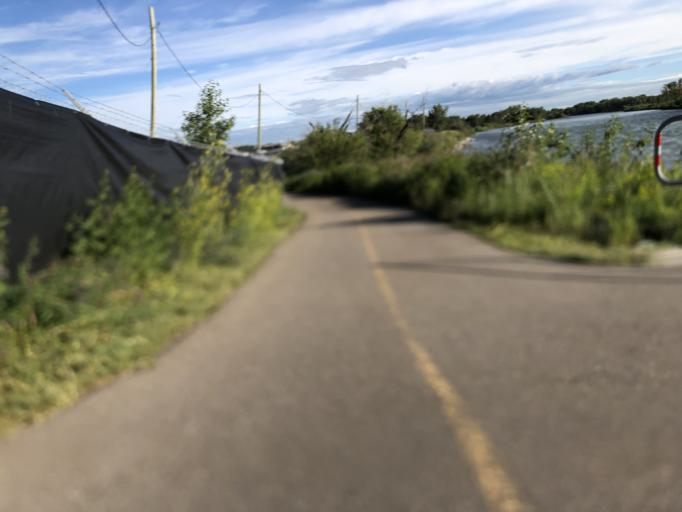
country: CA
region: Alberta
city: Calgary
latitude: 50.9562
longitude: -114.0237
